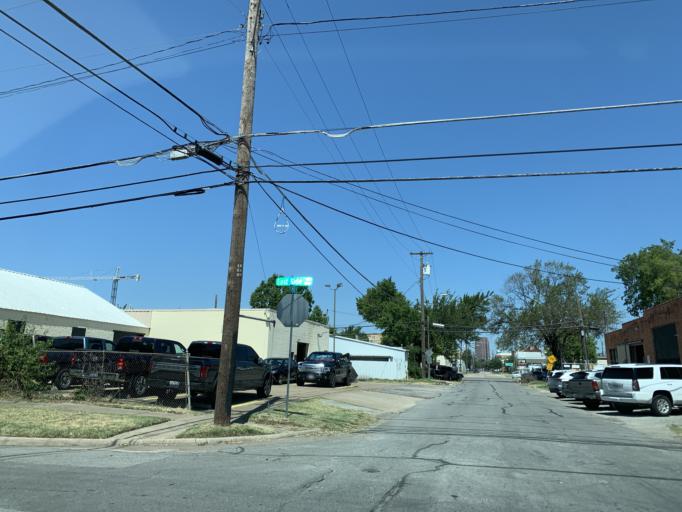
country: US
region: Texas
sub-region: Dallas County
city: Dallas
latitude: 32.7870
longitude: -96.7710
